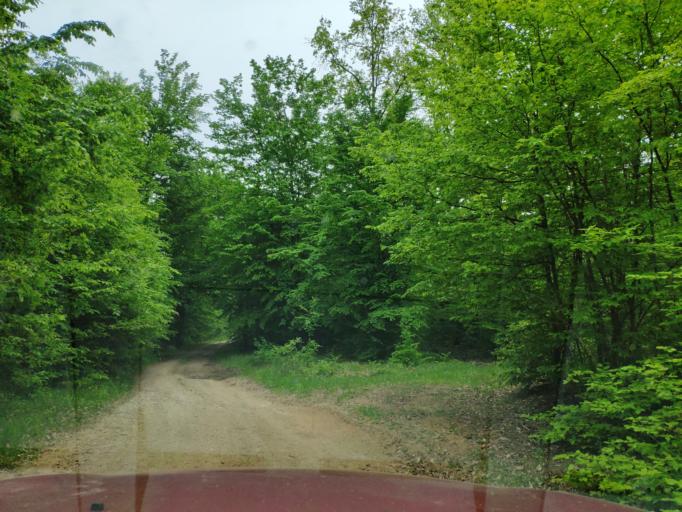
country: HU
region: Borsod-Abauj-Zemplen
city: Putnok
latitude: 48.4986
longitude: 20.3051
